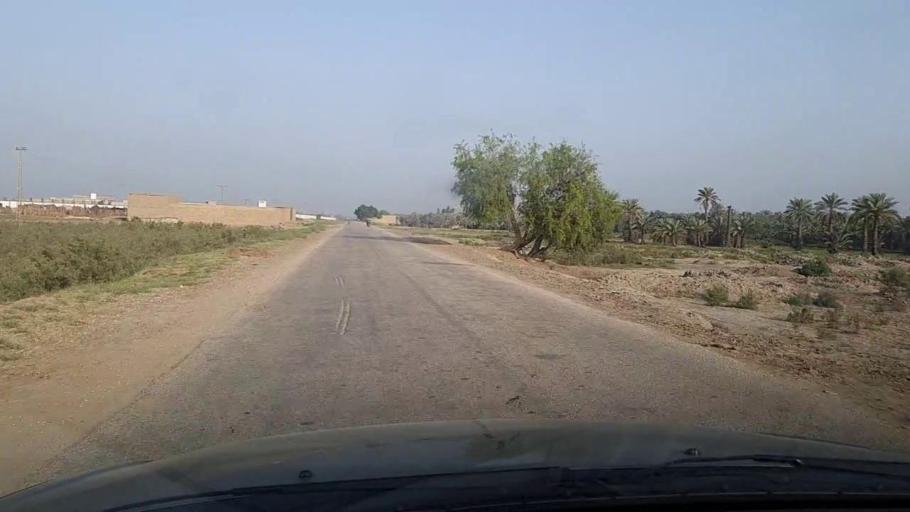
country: PK
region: Sindh
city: Khairpur
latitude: 27.5462
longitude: 68.7002
